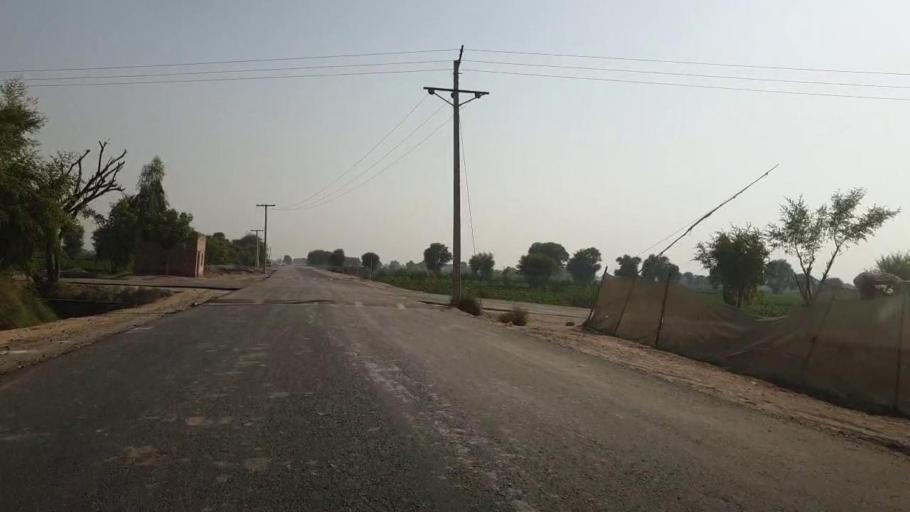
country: PK
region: Sindh
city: Bhan
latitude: 26.5339
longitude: 67.7885
